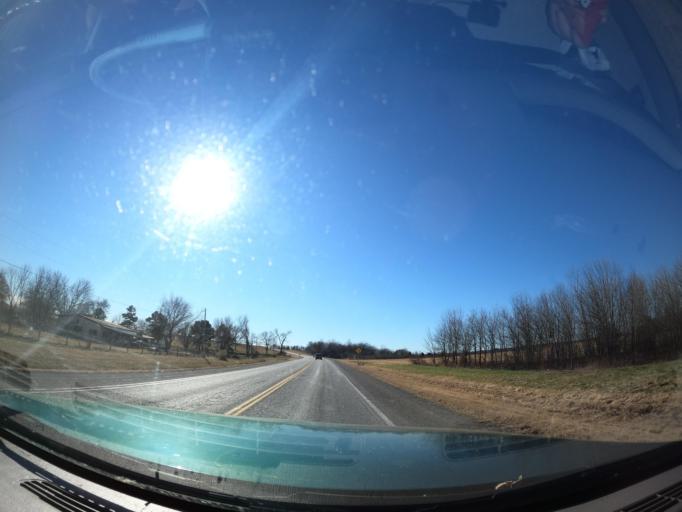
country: US
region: Oklahoma
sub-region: Muskogee County
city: Haskell
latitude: 35.8679
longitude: -95.6731
